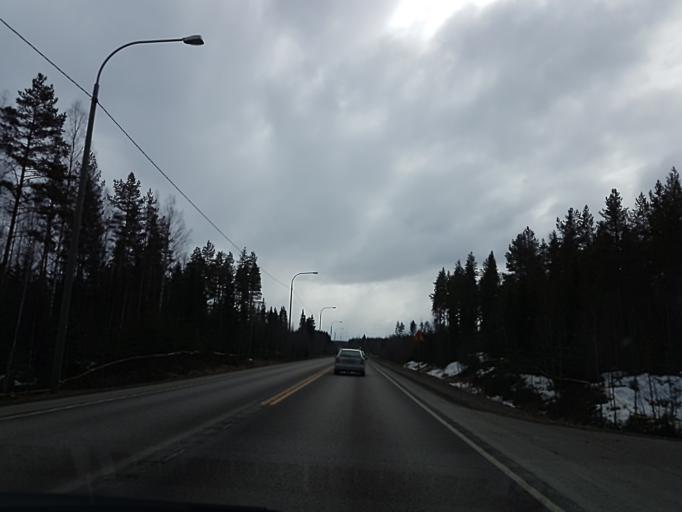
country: FI
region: Northern Savo
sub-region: Varkaus
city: Leppaevirta
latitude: 62.4265
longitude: 27.8157
